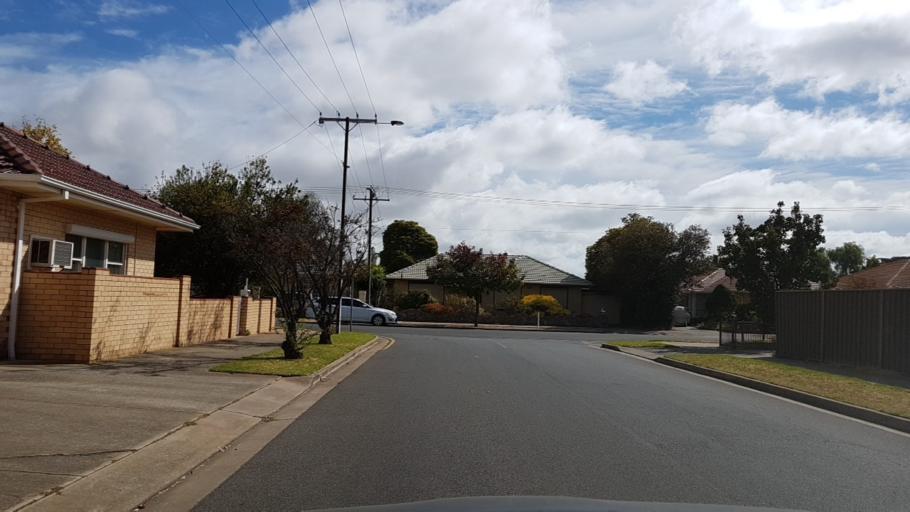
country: AU
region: South Australia
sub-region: Marion
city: Plympton Park
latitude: -34.9906
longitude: 138.5510
